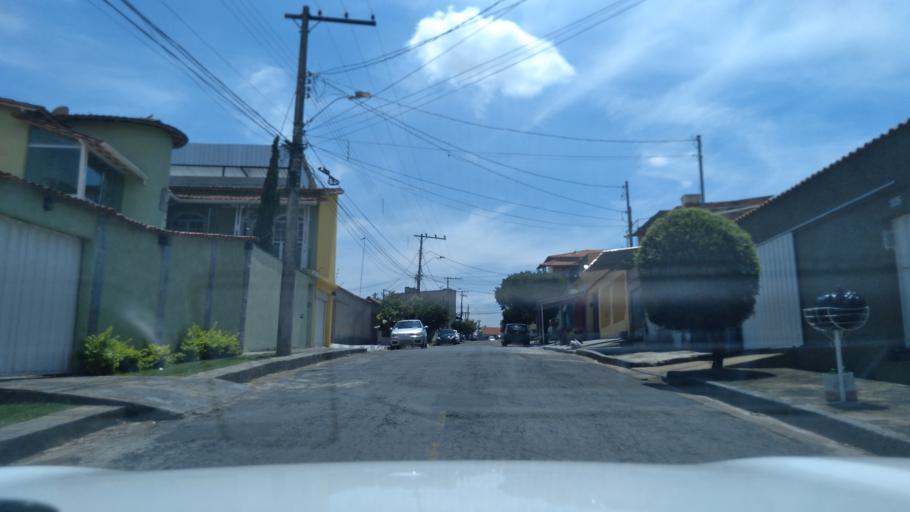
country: BR
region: Minas Gerais
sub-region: Contagem
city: Contagem
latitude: -19.9003
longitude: -44.0159
